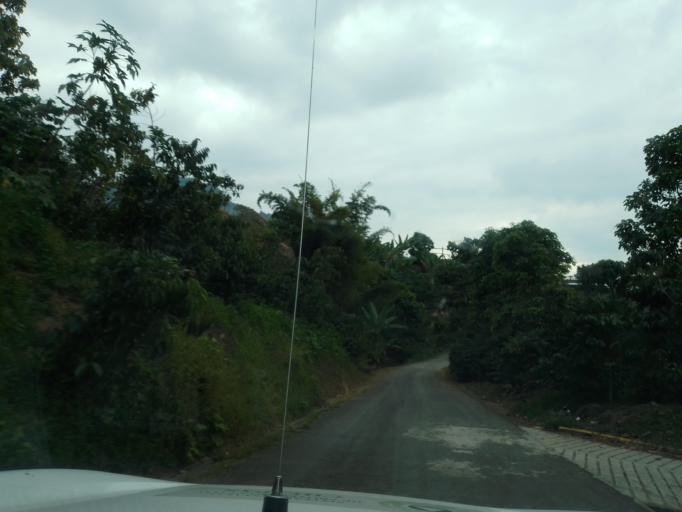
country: MX
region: Chiapas
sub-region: Union Juarez
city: Santo Domingo
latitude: 15.0544
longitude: -92.1252
